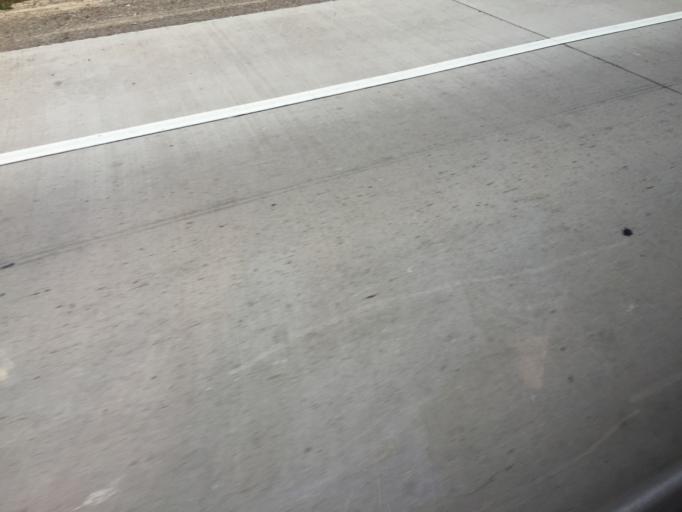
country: KZ
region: Ongtustik Qazaqstan
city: Temirlanovka
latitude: 42.8370
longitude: 69.1135
